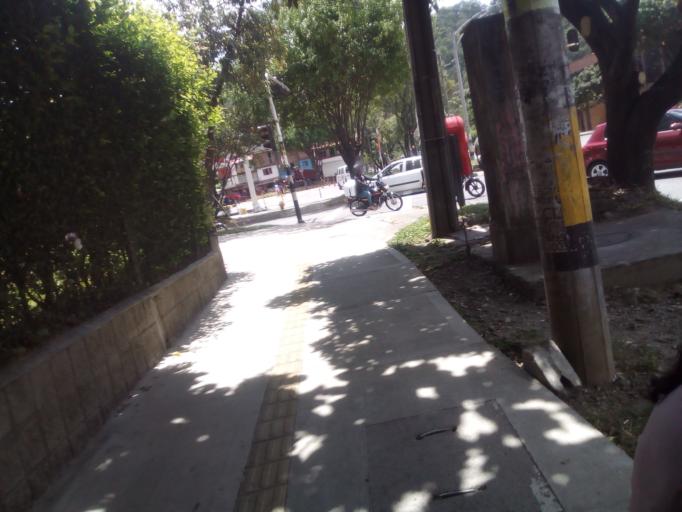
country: CO
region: Antioquia
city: Medellin
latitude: 6.2602
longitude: -75.5852
